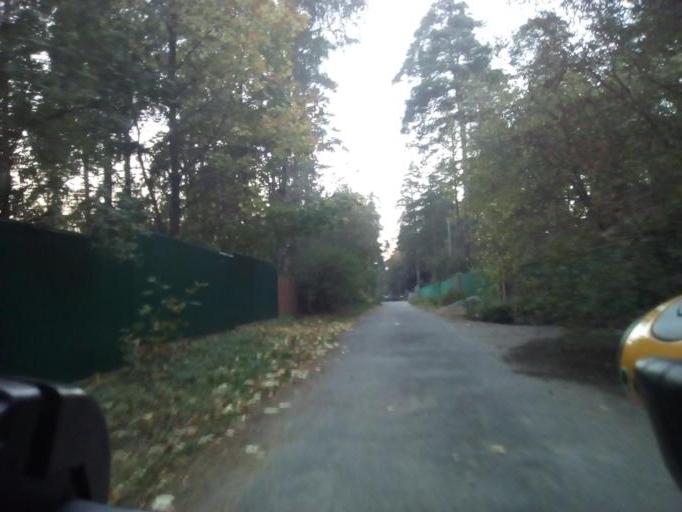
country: RU
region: Moskovskaya
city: Kratovo
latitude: 55.5977
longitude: 38.1841
